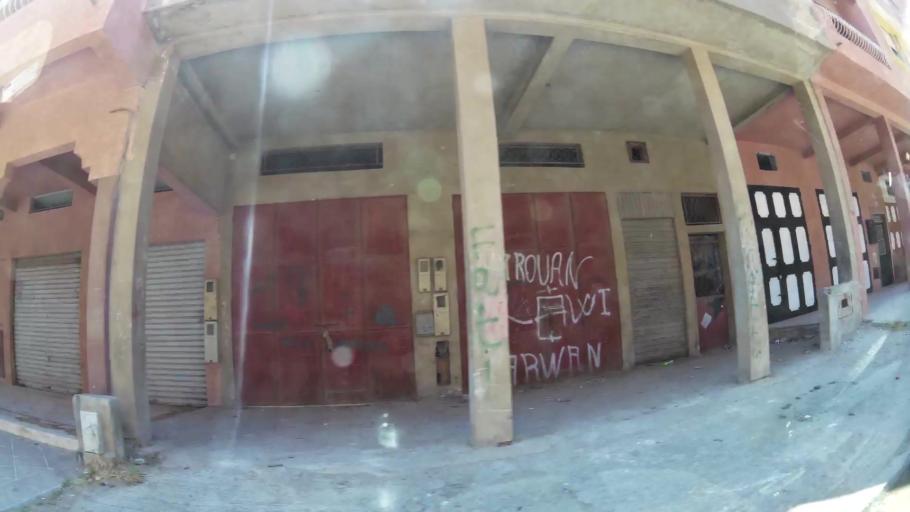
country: MA
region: Gharb-Chrarda-Beni Hssen
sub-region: Kenitra Province
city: Kenitra
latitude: 34.2530
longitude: -6.6187
